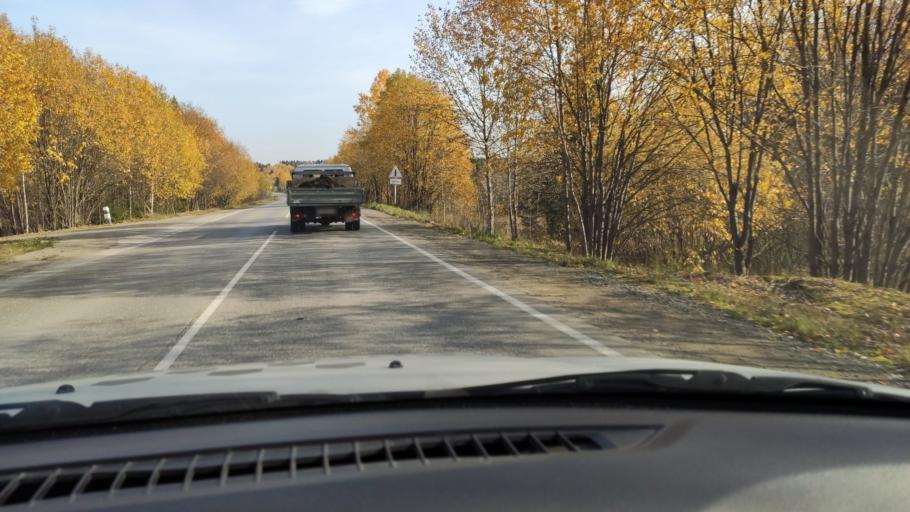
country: RU
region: Perm
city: Novyye Lyady
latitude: 58.0246
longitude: 56.6693
